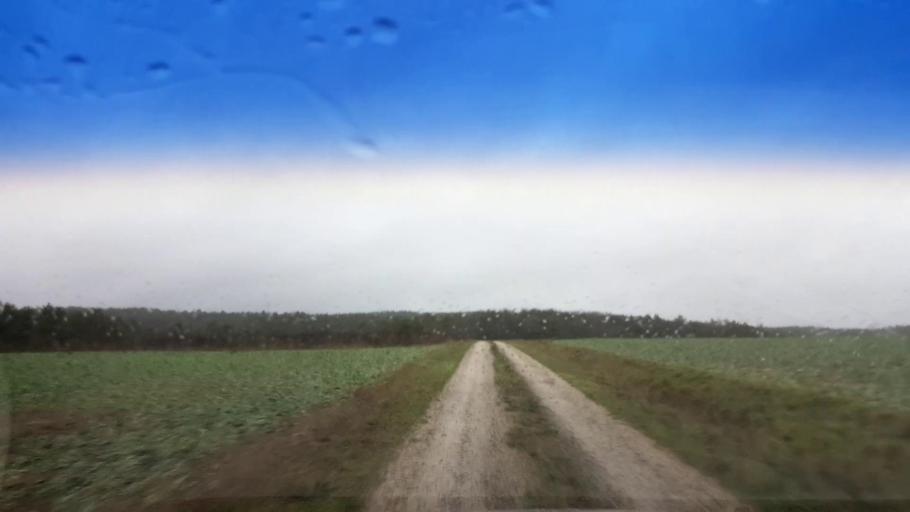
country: DE
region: Bavaria
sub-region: Upper Franconia
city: Lauter
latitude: 49.9508
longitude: 10.7682
